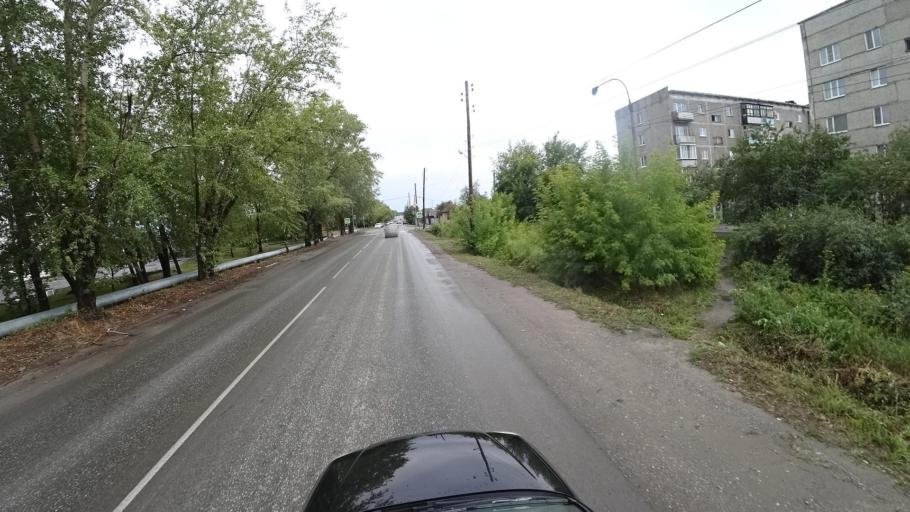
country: RU
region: Sverdlovsk
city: Kamyshlov
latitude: 56.8433
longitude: 62.7201
